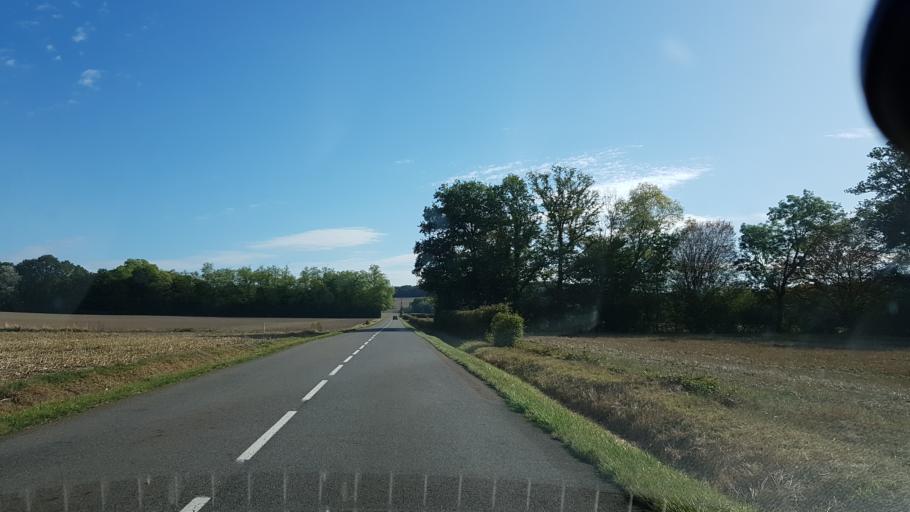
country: FR
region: Bourgogne
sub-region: Departement de la Nievre
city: Neuvy-sur-Loire
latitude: 47.5468
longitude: 2.9620
